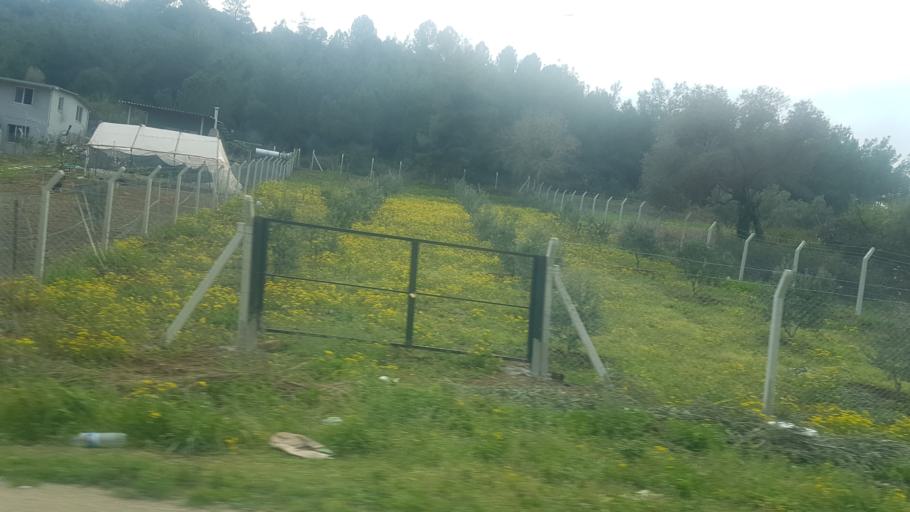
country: TR
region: Mersin
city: Yenice
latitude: 37.0871
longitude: 35.1637
